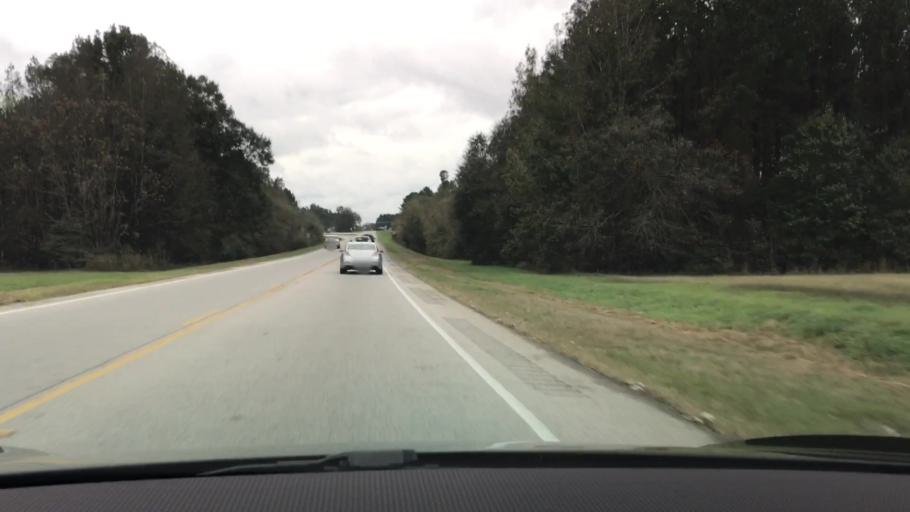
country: US
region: Georgia
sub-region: Jefferson County
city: Wadley
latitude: 32.8967
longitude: -82.4006
